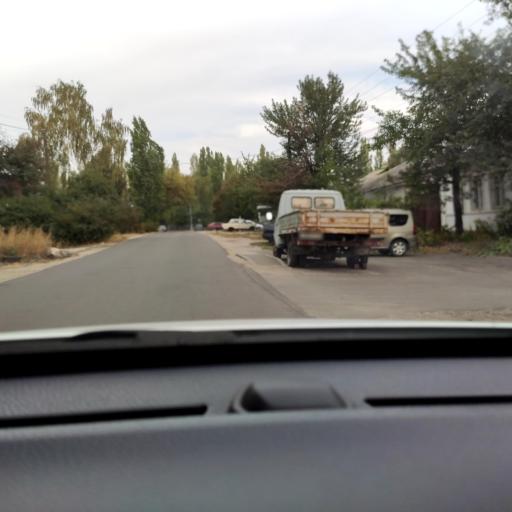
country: RU
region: Voronezj
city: Voronezh
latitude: 51.7008
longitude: 39.1685
